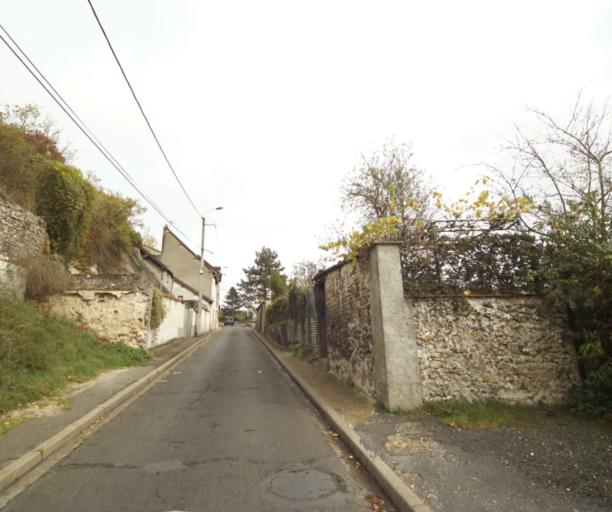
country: FR
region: Centre
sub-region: Departement d'Eure-et-Loir
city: Dreux
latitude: 48.7405
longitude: 1.3692
